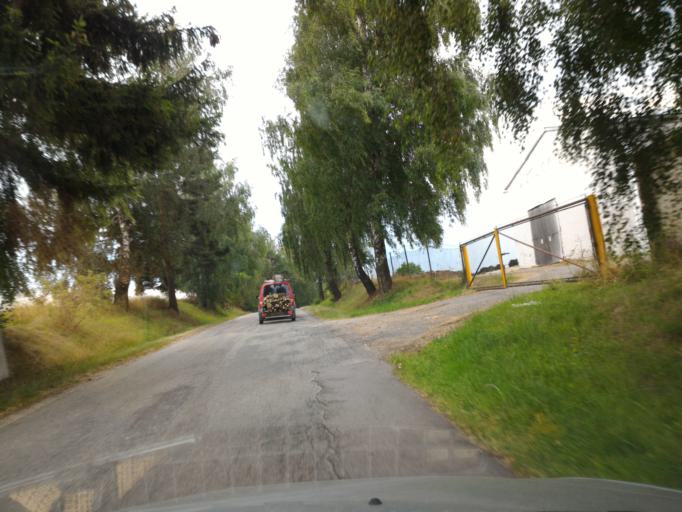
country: CZ
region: Vysocina
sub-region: Okres Jihlava
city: Trest'
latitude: 49.2444
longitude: 15.4491
